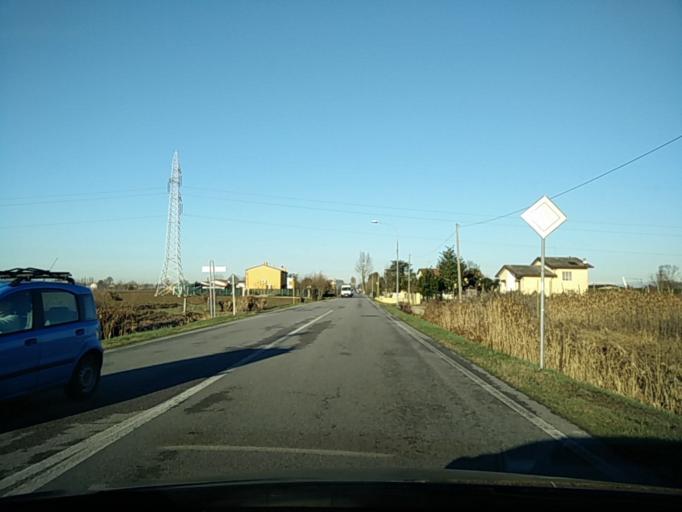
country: IT
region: Veneto
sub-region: Provincia di Venezia
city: Arino
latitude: 45.4528
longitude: 12.0479
